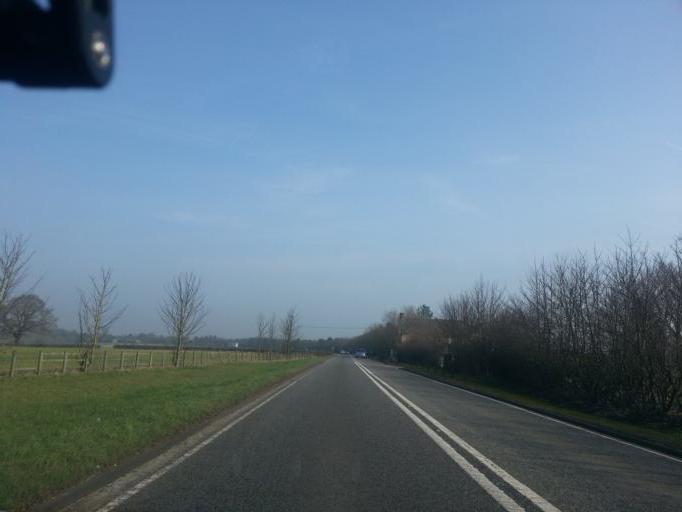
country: GB
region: England
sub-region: Oxfordshire
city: Faringdon
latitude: 51.6302
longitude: -1.6083
